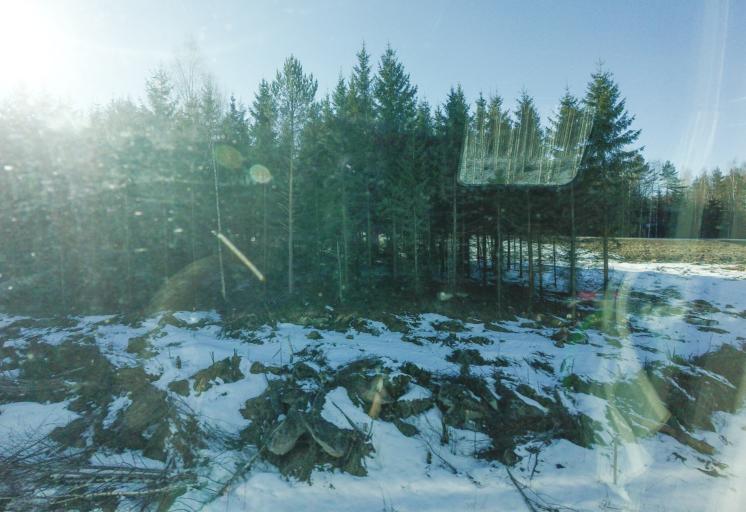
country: FI
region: South Karelia
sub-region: Imatra
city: Parikkala
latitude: 61.5155
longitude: 29.5117
